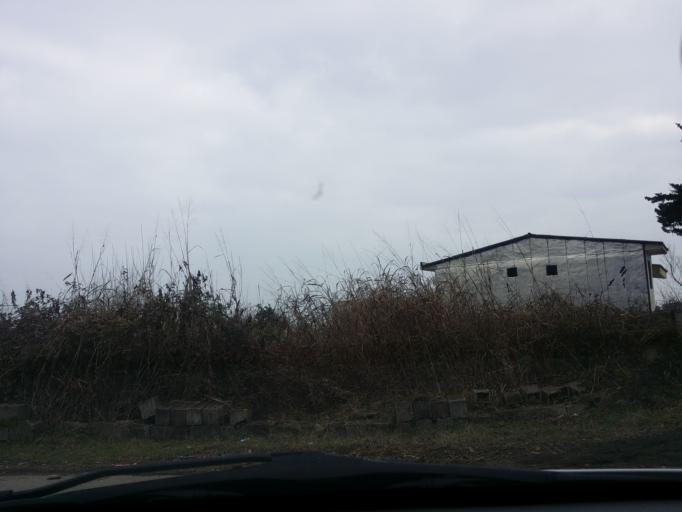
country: IR
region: Mazandaran
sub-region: Nowshahr
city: Nowshahr
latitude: 36.6492
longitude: 51.4719
